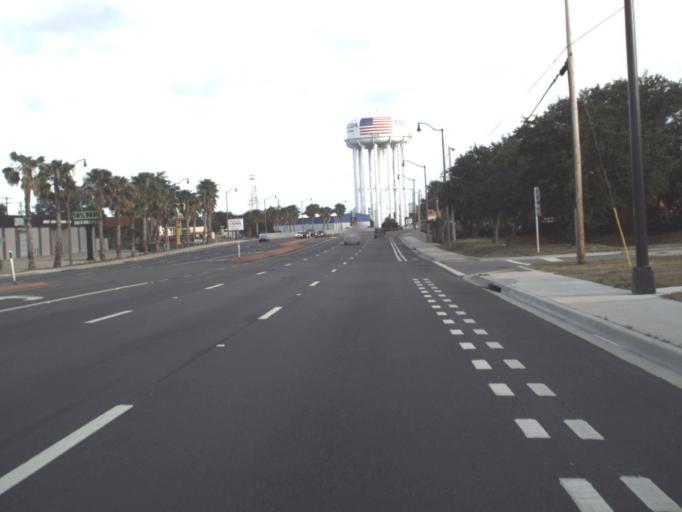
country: US
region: Florida
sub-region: Brevard County
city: Rockledge
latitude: 28.3615
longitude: -80.7339
